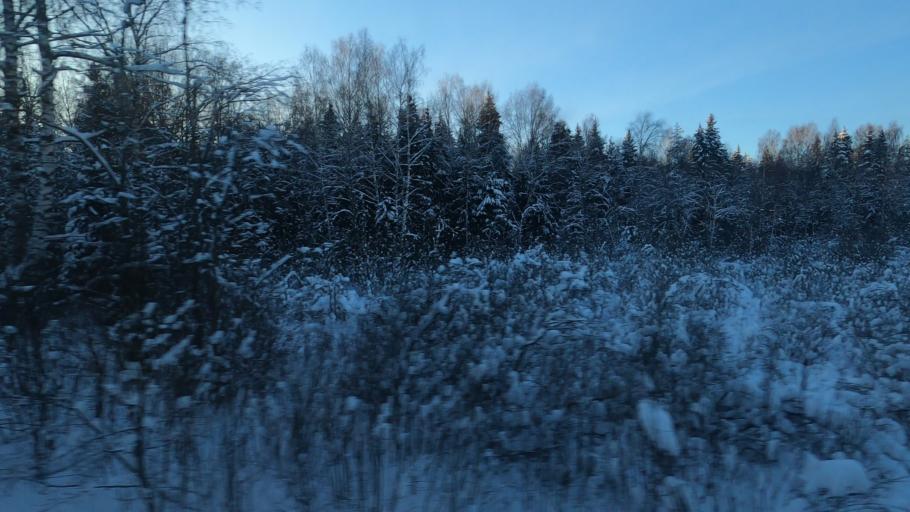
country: RU
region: Moskovskaya
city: Novo-Nikol'skoye
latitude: 56.5587
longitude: 37.5654
